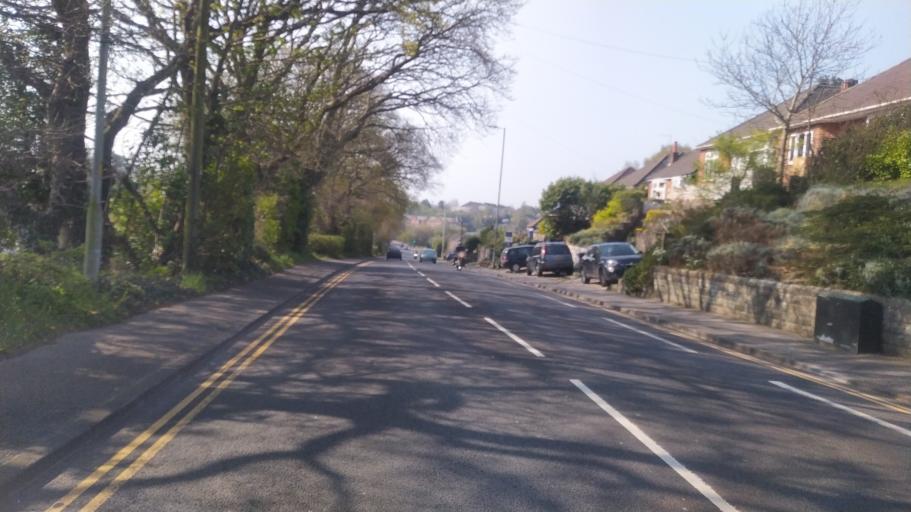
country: GB
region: England
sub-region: Dorset
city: Parkstone
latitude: 50.7447
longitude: -1.9111
